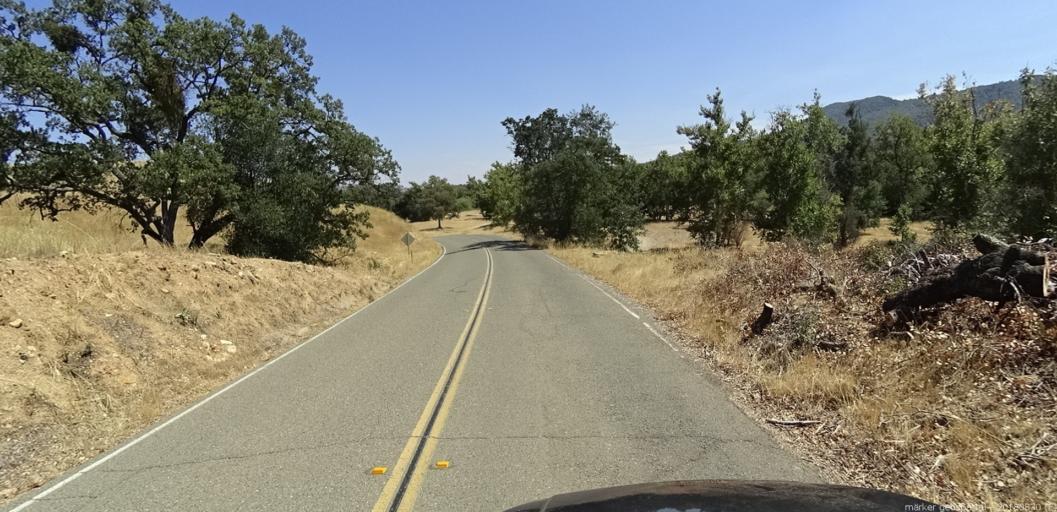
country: US
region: California
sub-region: Monterey County
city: King City
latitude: 35.9764
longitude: -121.3432
